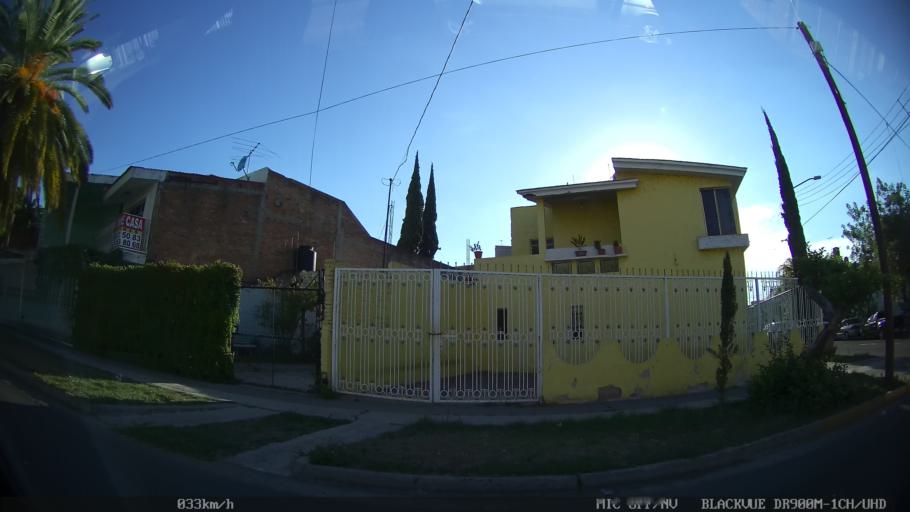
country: MX
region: Jalisco
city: Tlaquepaque
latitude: 20.7022
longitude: -103.2968
